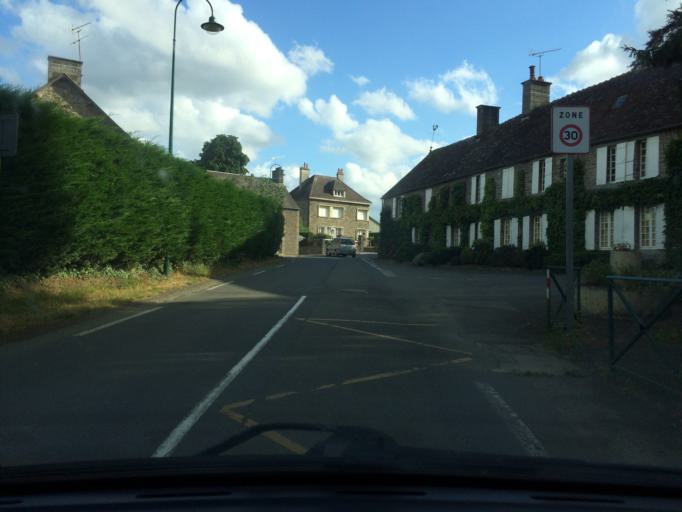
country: FR
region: Lower Normandy
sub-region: Departement du Calvados
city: Clecy
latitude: 48.8542
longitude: -0.4108
